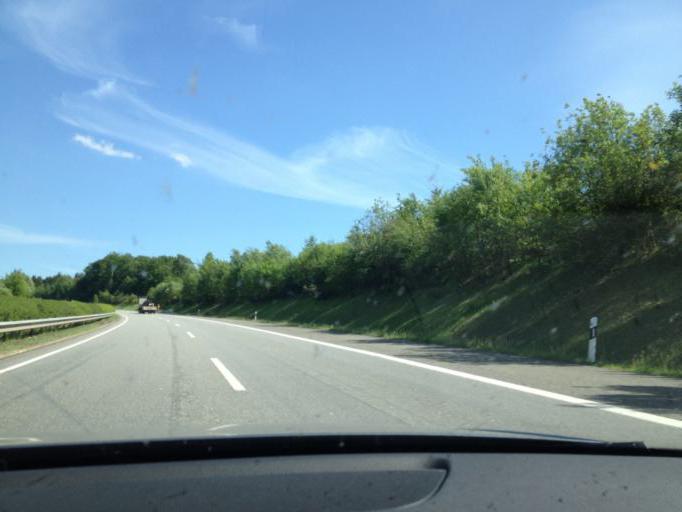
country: DE
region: Rheinland-Pfalz
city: Bergweiler
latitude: 49.9812
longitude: 6.7983
